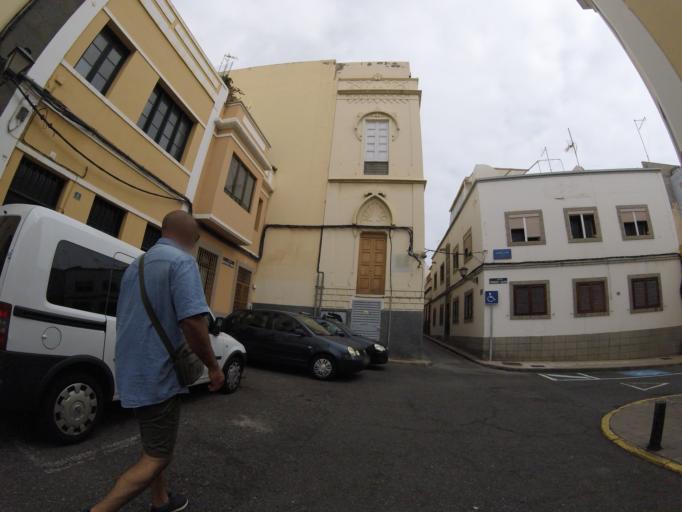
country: ES
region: Canary Islands
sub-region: Provincia de Las Palmas
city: Las Palmas de Gran Canaria
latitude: 28.0978
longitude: -15.4157
